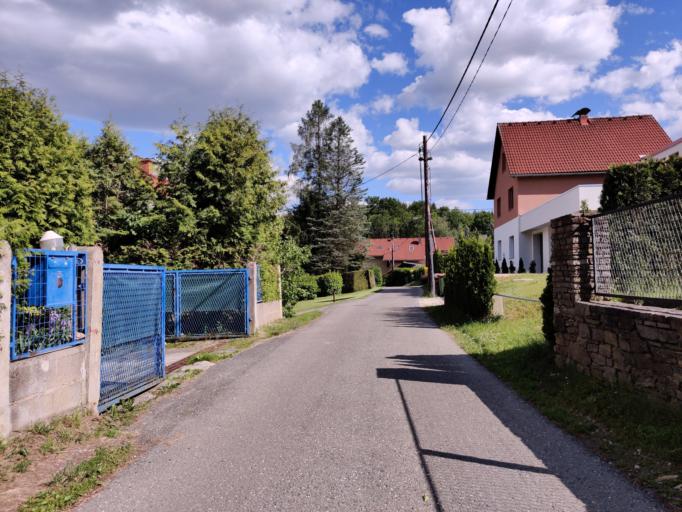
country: AT
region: Styria
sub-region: Politischer Bezirk Graz-Umgebung
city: Thal
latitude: 47.0555
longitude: 15.3715
